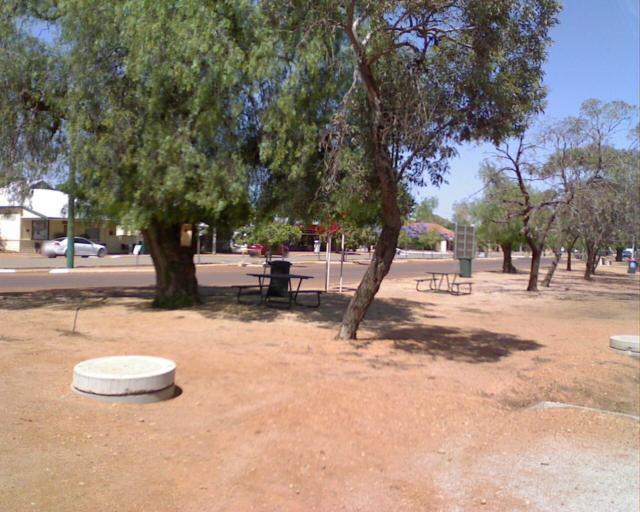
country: AU
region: Western Australia
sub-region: Merredin
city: Merredin
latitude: -30.9142
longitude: 118.2095
